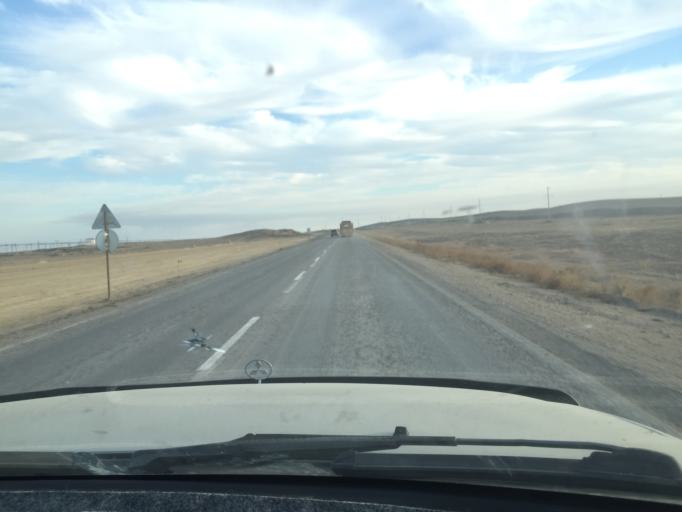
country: KZ
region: Almaty Oblysy
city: Ulken
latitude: 45.1812
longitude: 73.9244
